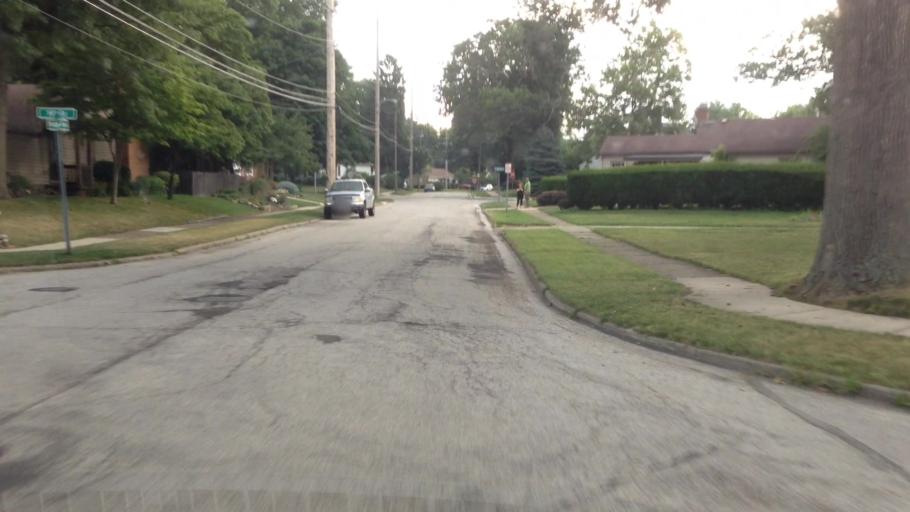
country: US
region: Ohio
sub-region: Summit County
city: Cuyahoga Falls
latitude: 41.1397
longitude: -81.5052
